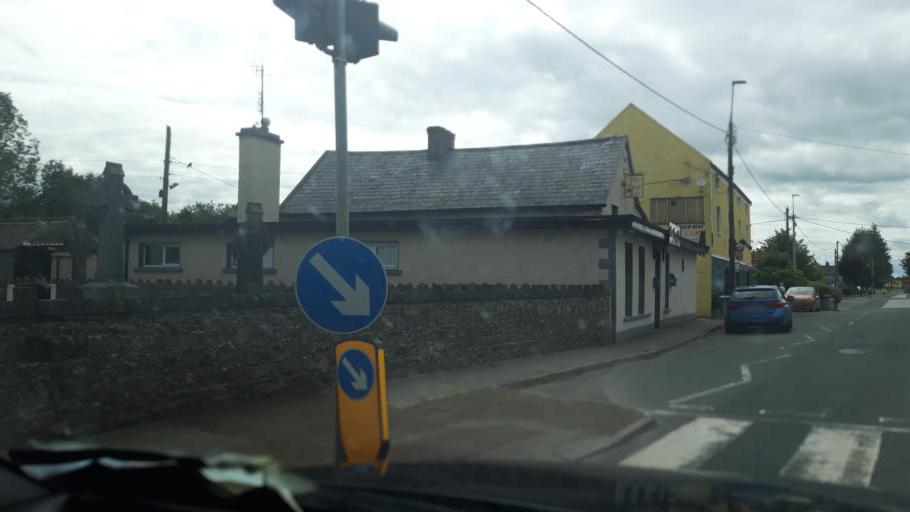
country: IE
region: Munster
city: Carrick-on-Suir
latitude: 52.4460
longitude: -7.4693
